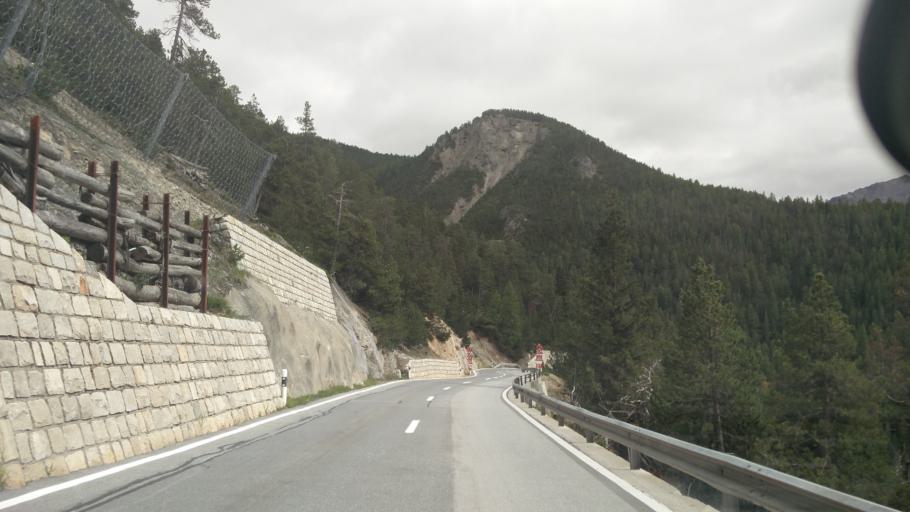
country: CH
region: Grisons
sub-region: Inn District
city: Zernez
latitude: 46.6552
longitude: 10.1777
